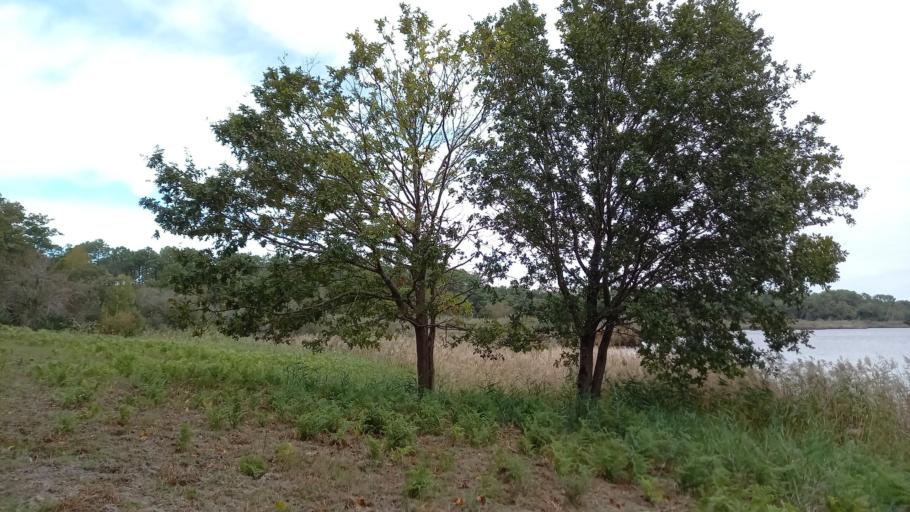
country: FR
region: Aquitaine
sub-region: Departement de la Gironde
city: Lacanau
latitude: 45.0360
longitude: -1.1457
